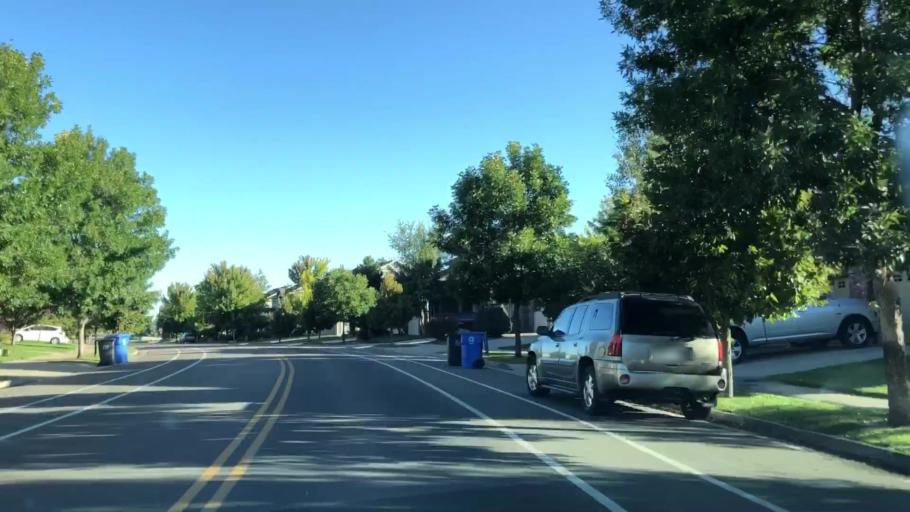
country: US
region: Colorado
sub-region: Larimer County
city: Loveland
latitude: 40.4580
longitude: -105.0316
